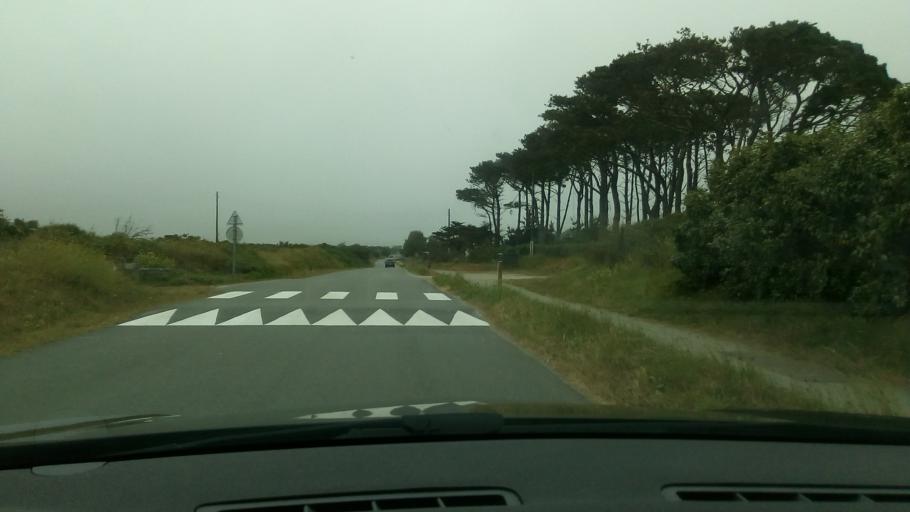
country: FR
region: Brittany
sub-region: Departement du Finistere
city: Le Conquet
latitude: 48.3683
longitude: -4.7585
